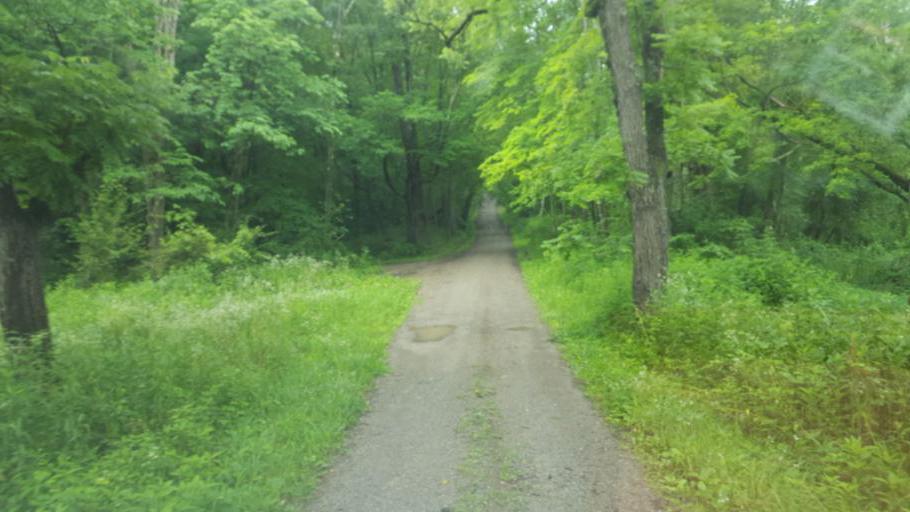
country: US
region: Ohio
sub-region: Columbiana County
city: Salineville
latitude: 40.5586
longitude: -80.8047
